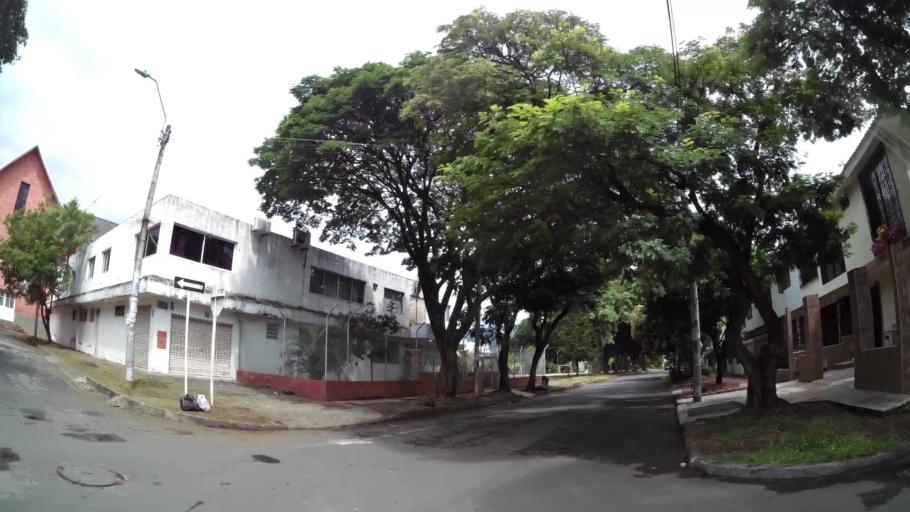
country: CO
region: Valle del Cauca
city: Cali
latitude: 3.3959
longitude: -76.5487
